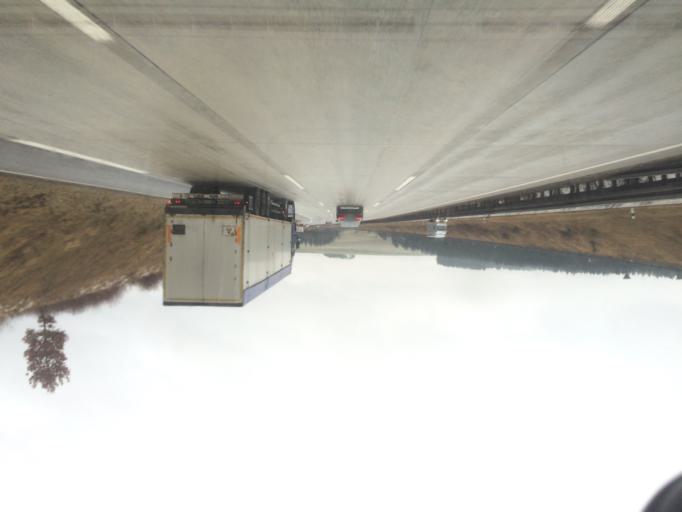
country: DE
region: Thuringia
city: Birkenhugel
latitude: 50.4444
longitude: 11.8028
